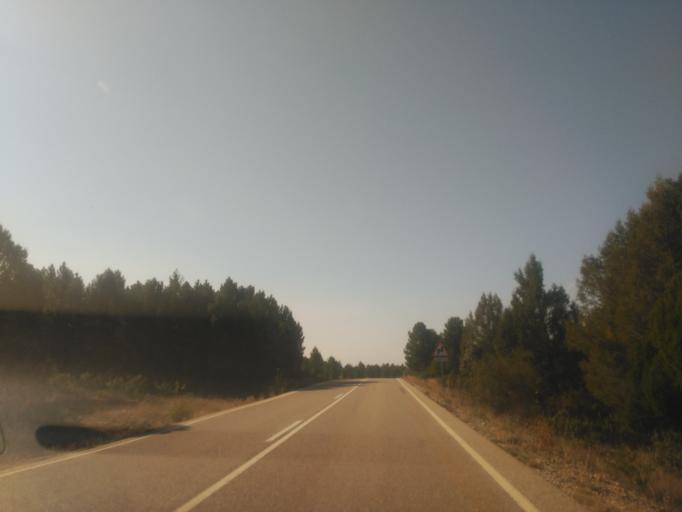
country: ES
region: Castille and Leon
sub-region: Provincia de Soria
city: Herrera de Soria
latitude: 41.7682
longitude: -3.0307
